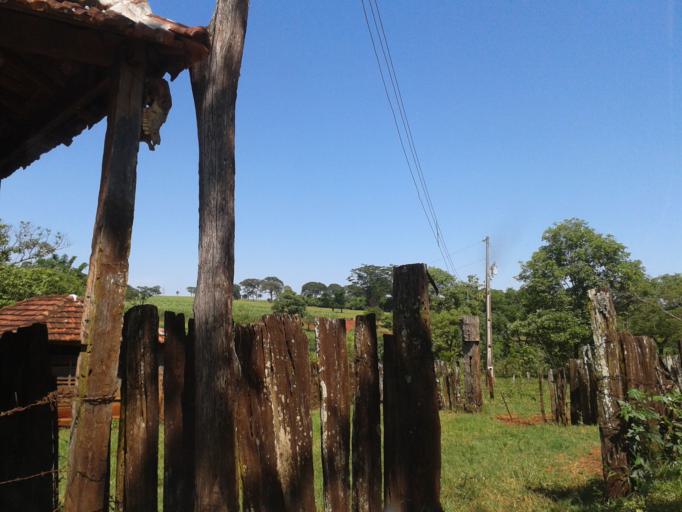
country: BR
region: Minas Gerais
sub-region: Centralina
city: Centralina
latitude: -18.6352
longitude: -49.2958
